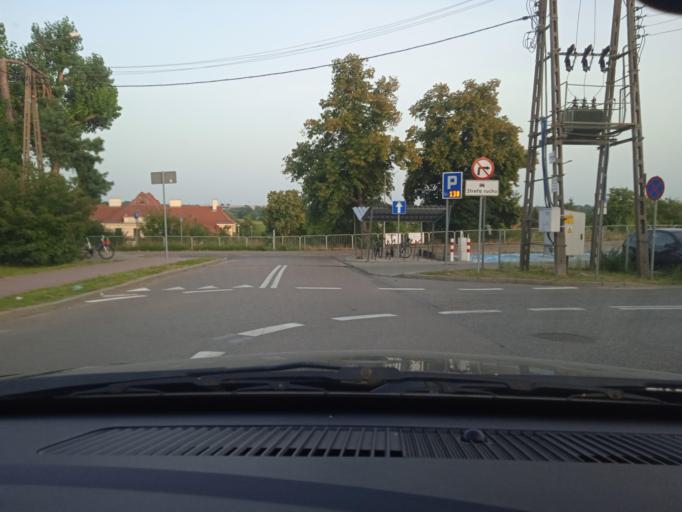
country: PL
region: Masovian Voivodeship
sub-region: Powiat nowodworski
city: Nowy Dwor Mazowiecki
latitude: 52.4438
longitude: 20.7021
